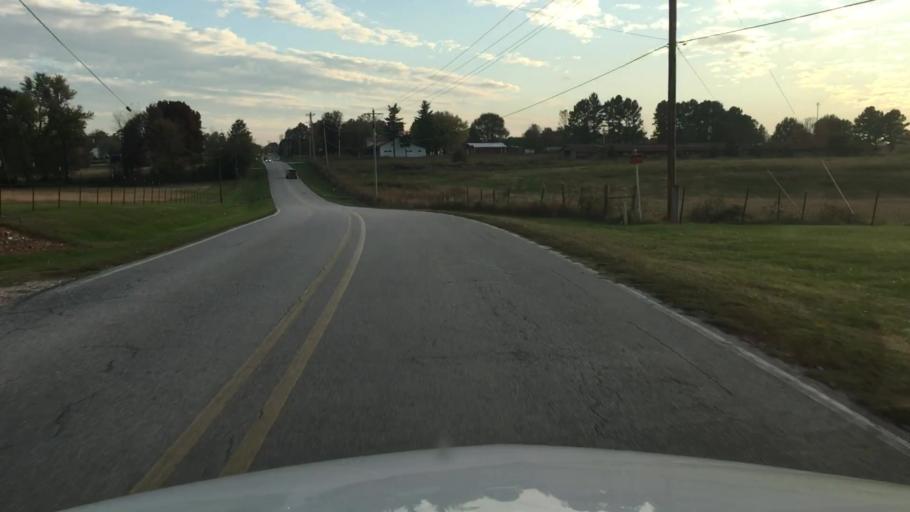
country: US
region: Arkansas
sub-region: Washington County
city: Tontitown
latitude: 36.1825
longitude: -94.2342
